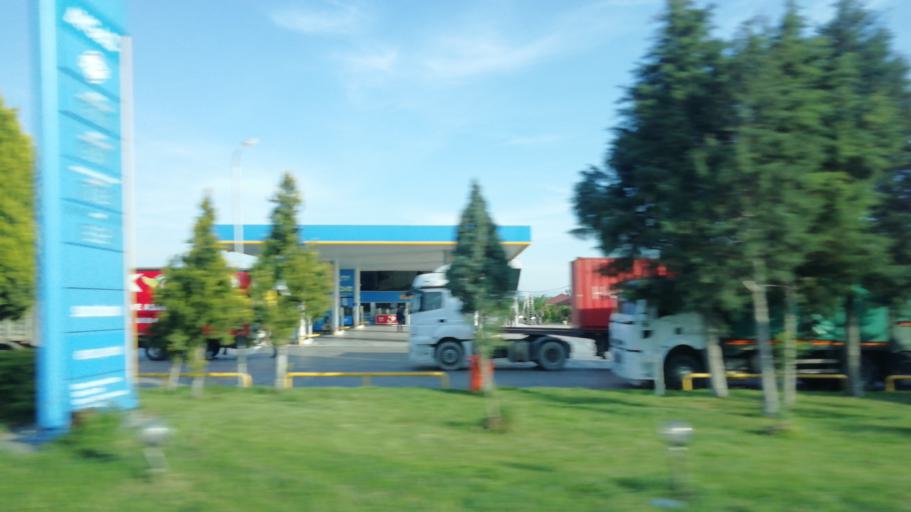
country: TR
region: Manisa
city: Saruhanli
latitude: 38.7328
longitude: 27.5867
